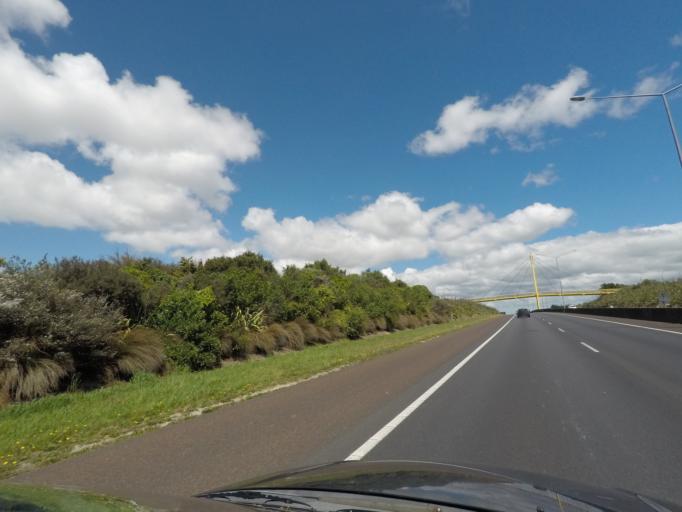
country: NZ
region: Auckland
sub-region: Auckland
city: Rosebank
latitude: -36.7946
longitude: 174.6487
